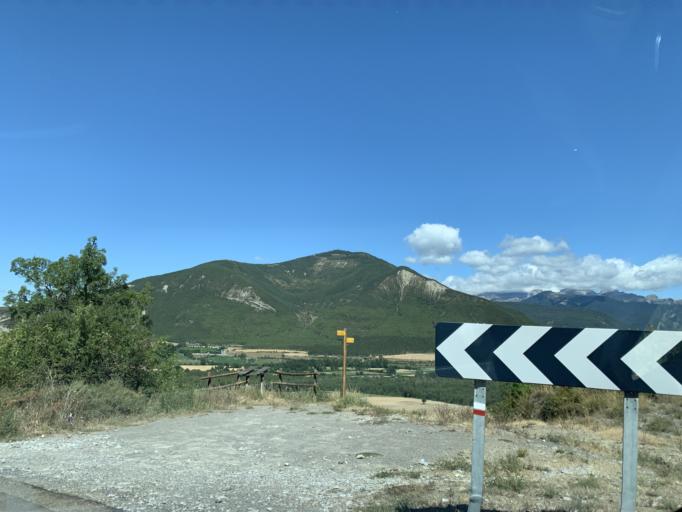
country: ES
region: Aragon
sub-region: Provincia de Huesca
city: Sabinanigo
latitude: 42.5468
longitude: -0.3179
